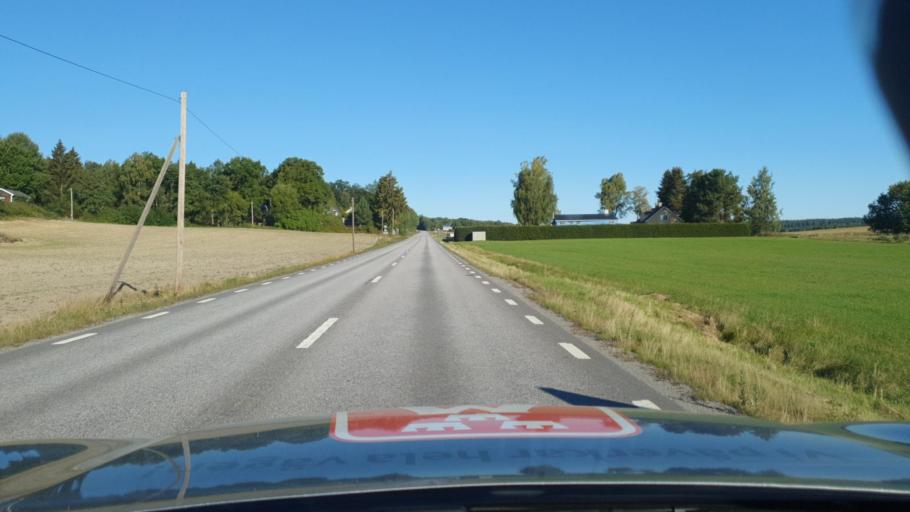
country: SE
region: OEstergoetland
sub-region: Finspangs Kommun
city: Finspang
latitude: 58.6467
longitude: 15.8194
